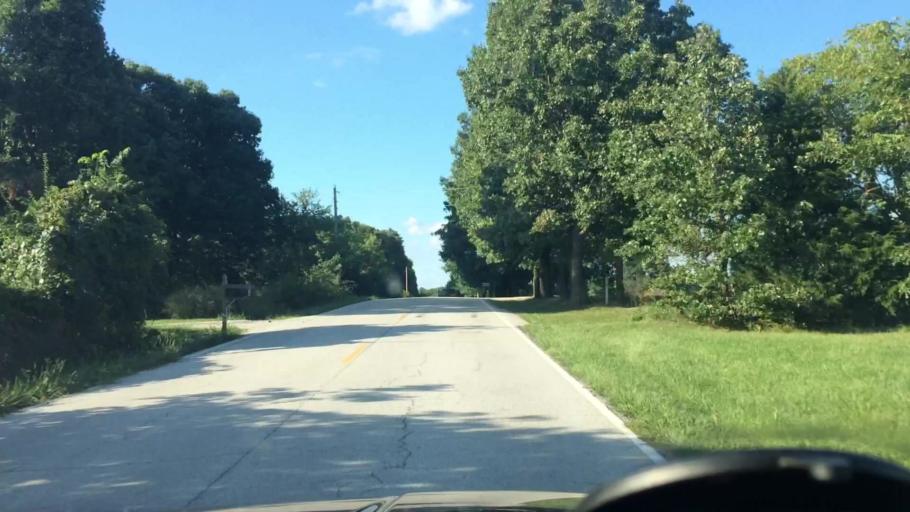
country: US
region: Missouri
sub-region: Greene County
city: Strafford
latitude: 37.2807
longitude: -93.0812
